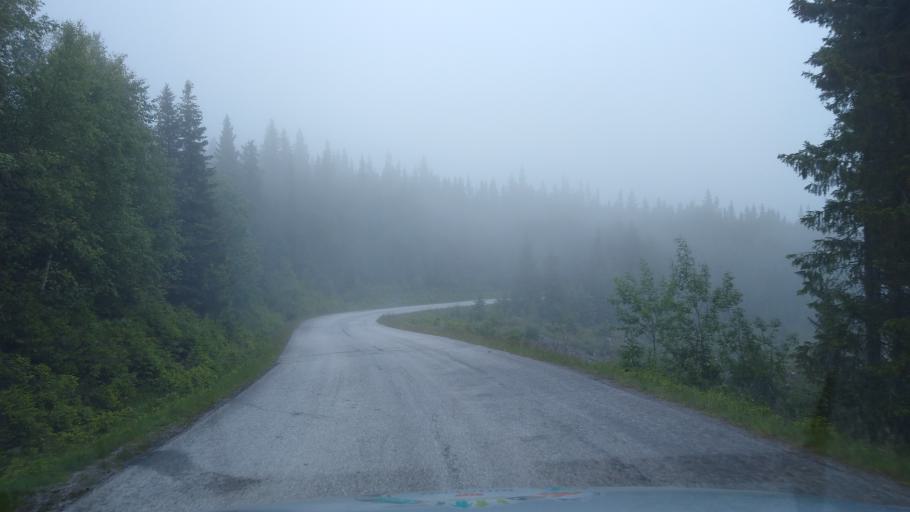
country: NO
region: Oppland
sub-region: Ringebu
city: Ringebu
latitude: 61.4912
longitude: 10.1298
